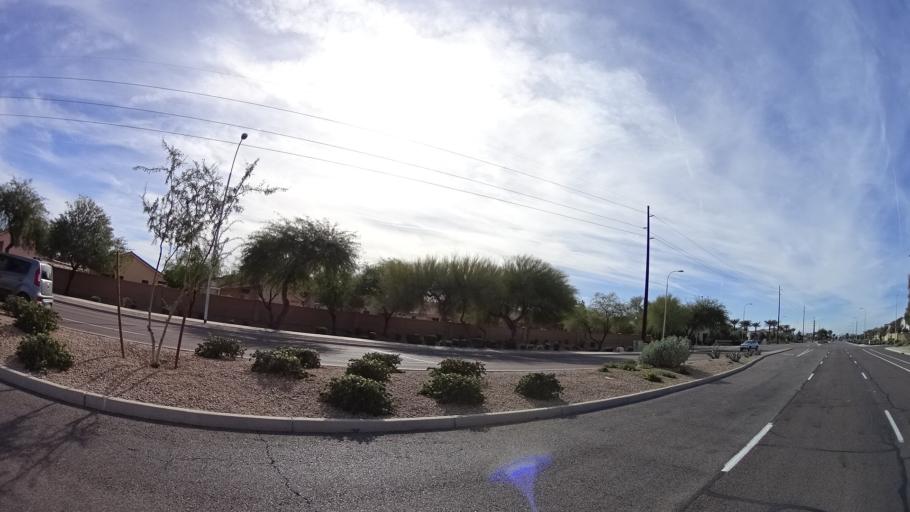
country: US
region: Arizona
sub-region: Maricopa County
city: Chandler
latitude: 33.2919
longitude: -111.8015
